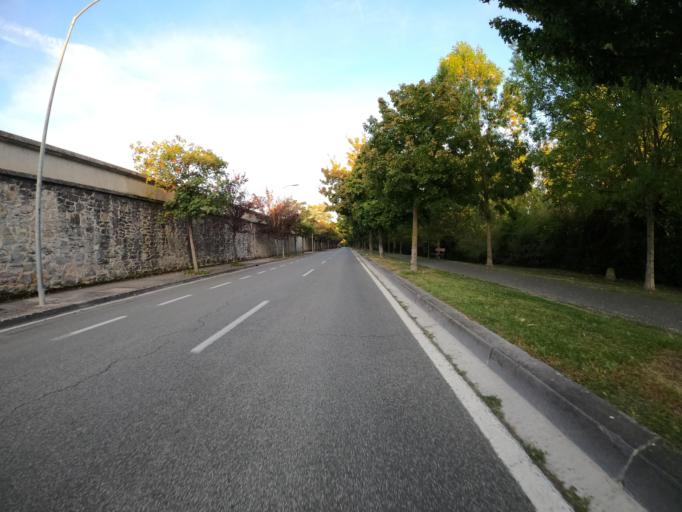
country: ES
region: Navarre
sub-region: Provincia de Navarra
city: Ermitagana
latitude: 42.8178
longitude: -1.6711
